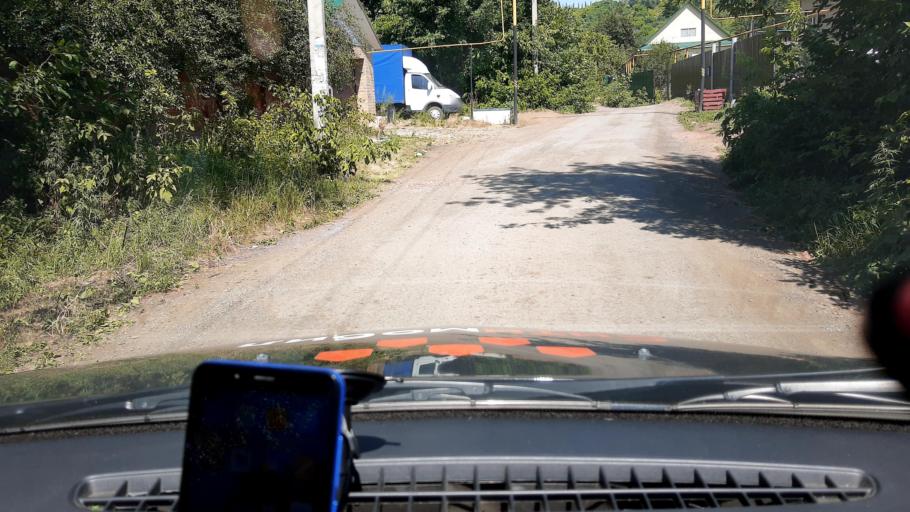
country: RU
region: Bashkortostan
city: Ufa
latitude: 54.7091
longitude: 55.9375
